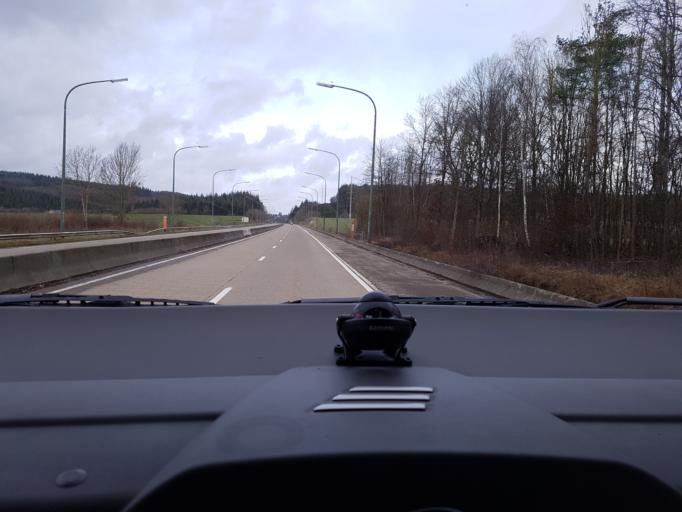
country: BE
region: Wallonia
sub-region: Province du Luxembourg
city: Marche-en-Famenne
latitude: 50.1918
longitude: 5.3706
